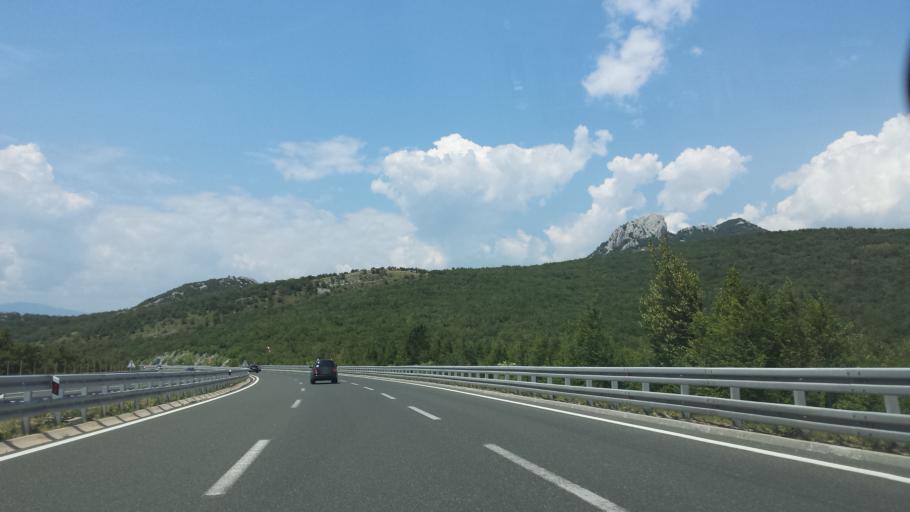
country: HR
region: Primorsko-Goranska
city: Krasica
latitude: 45.3613
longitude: 14.5730
